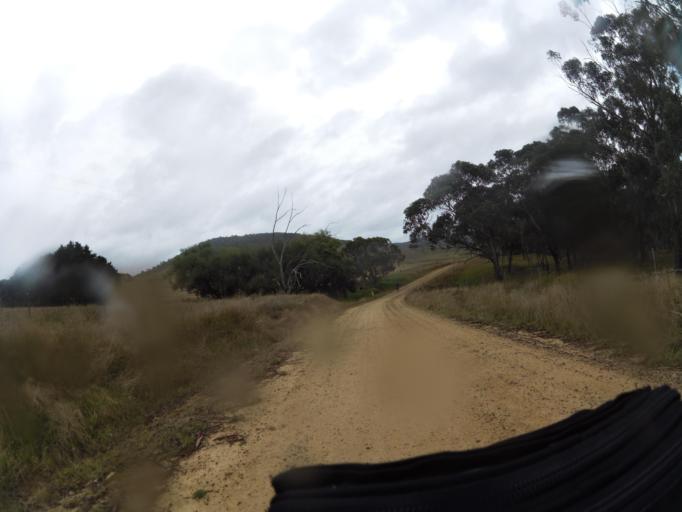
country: AU
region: New South Wales
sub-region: Greater Hume Shire
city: Holbrook
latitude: -36.2398
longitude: 147.6384
